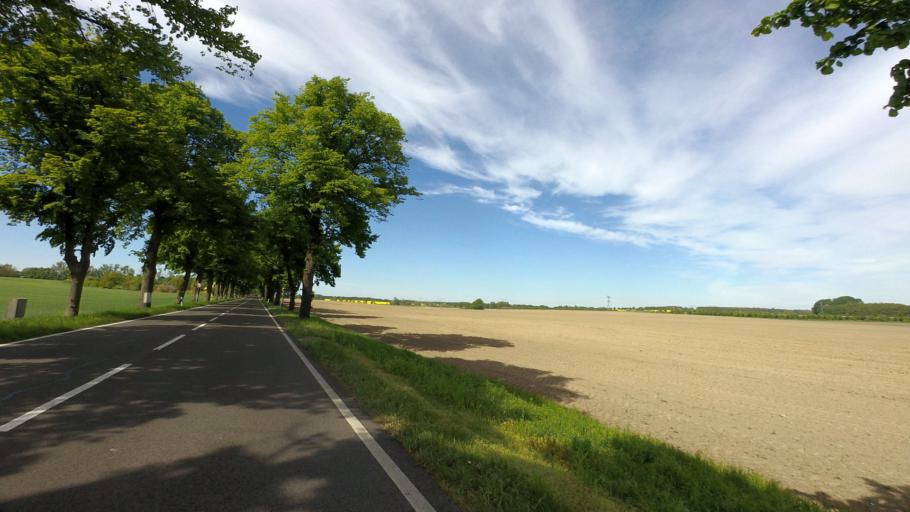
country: DE
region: Brandenburg
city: Rangsdorf
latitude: 52.3254
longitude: 13.4374
